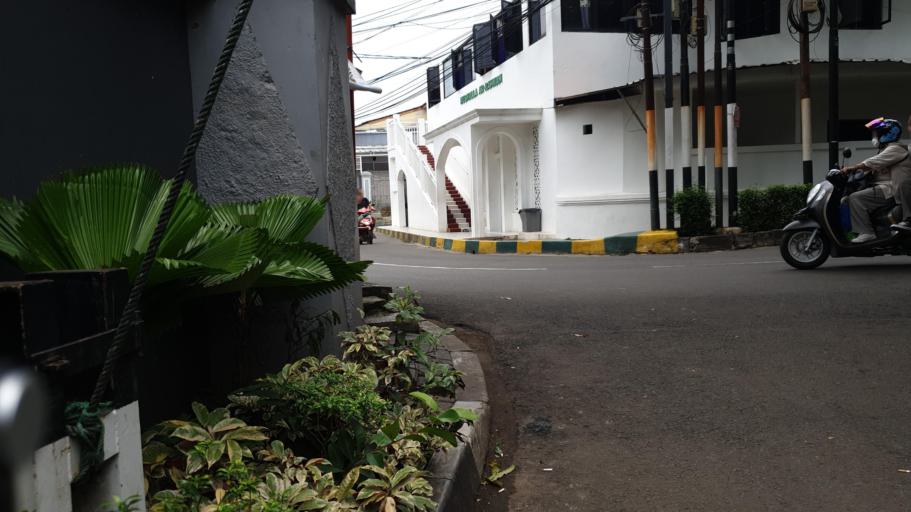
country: ID
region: West Java
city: Pamulang
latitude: -6.3070
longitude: 106.7804
